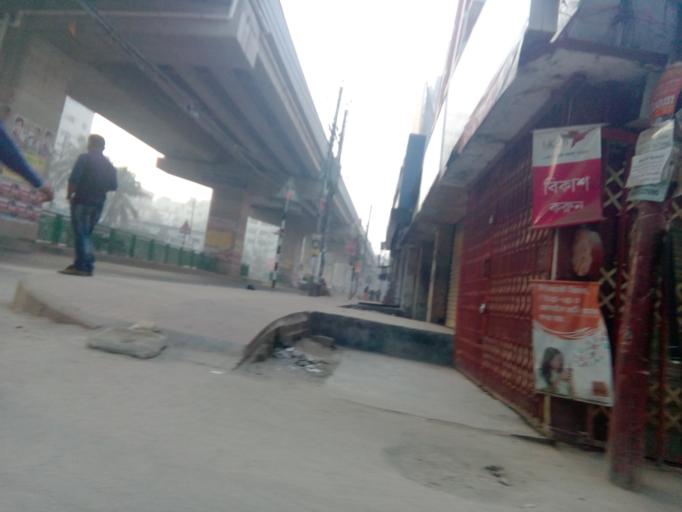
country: BD
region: Dhaka
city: Paltan
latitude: 23.7480
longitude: 90.4123
